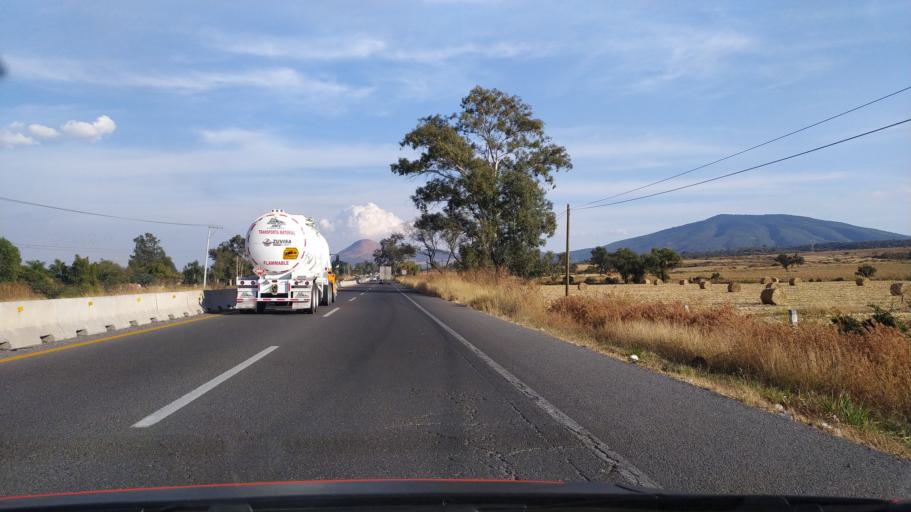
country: MX
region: Jalisco
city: Poncitlan
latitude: 20.3724
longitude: -102.9156
